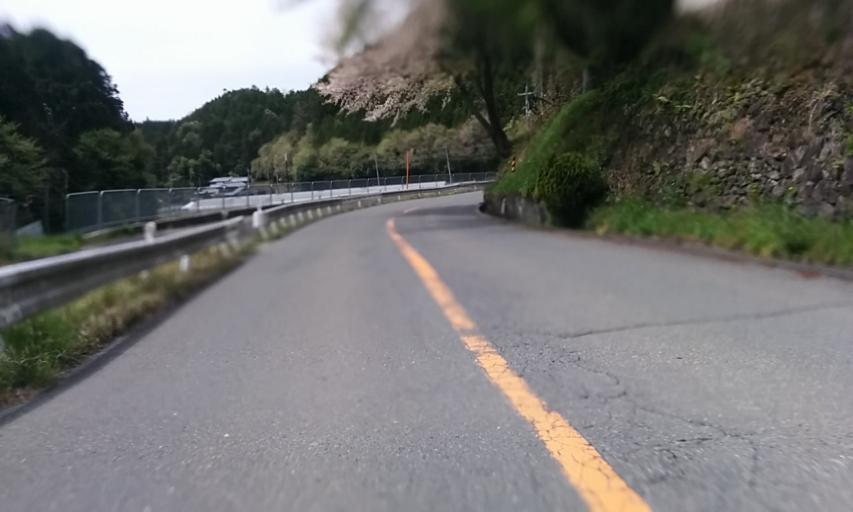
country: JP
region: Kyoto
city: Kameoka
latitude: 34.9699
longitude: 135.5822
